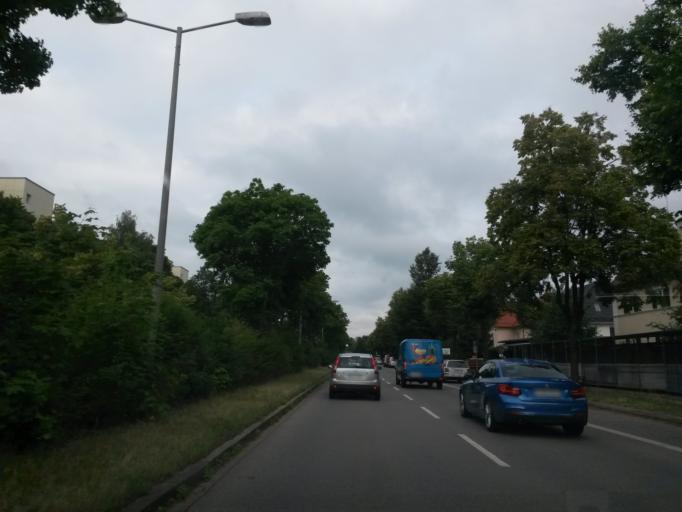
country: DE
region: Bavaria
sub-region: Upper Bavaria
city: Haar
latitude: 48.1074
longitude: 11.7304
